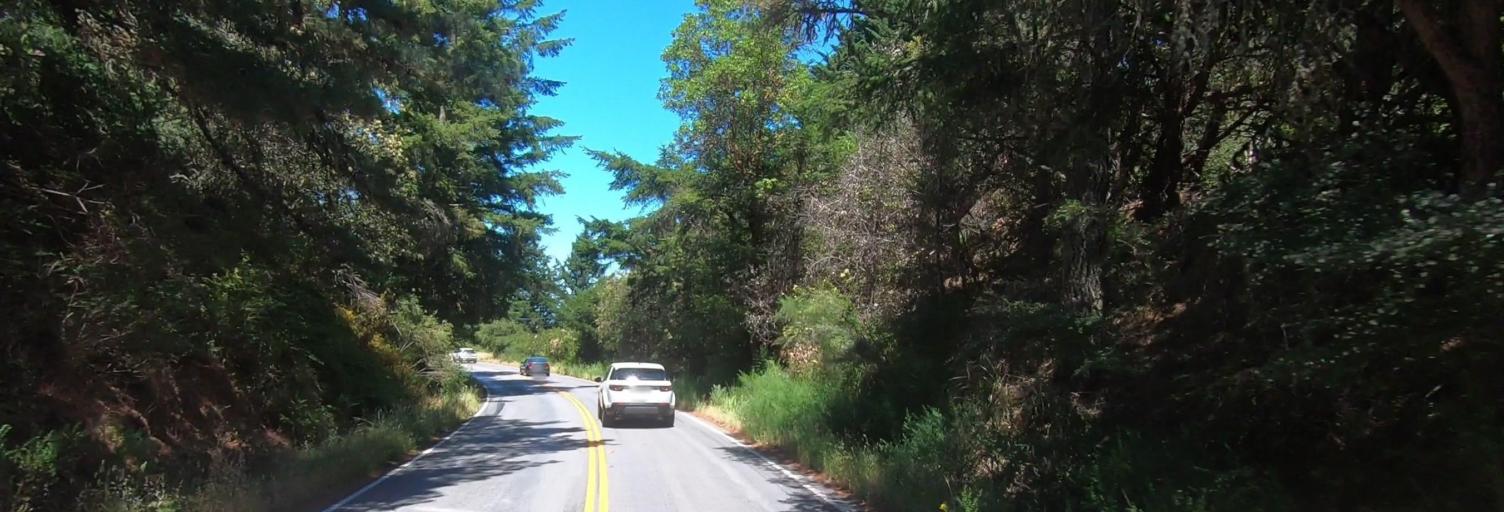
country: US
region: California
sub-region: San Mateo County
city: Highlands-Baywood Park
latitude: 37.4643
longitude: -122.3447
